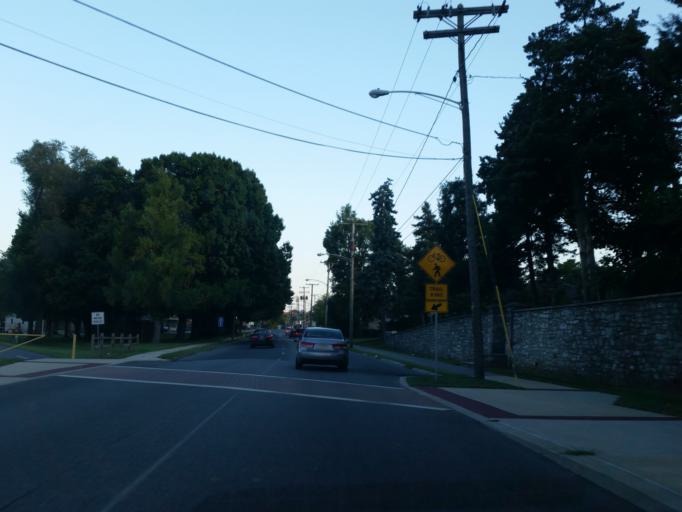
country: US
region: Pennsylvania
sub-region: Lebanon County
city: Pleasant Hill
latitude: 40.3329
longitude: -76.4271
